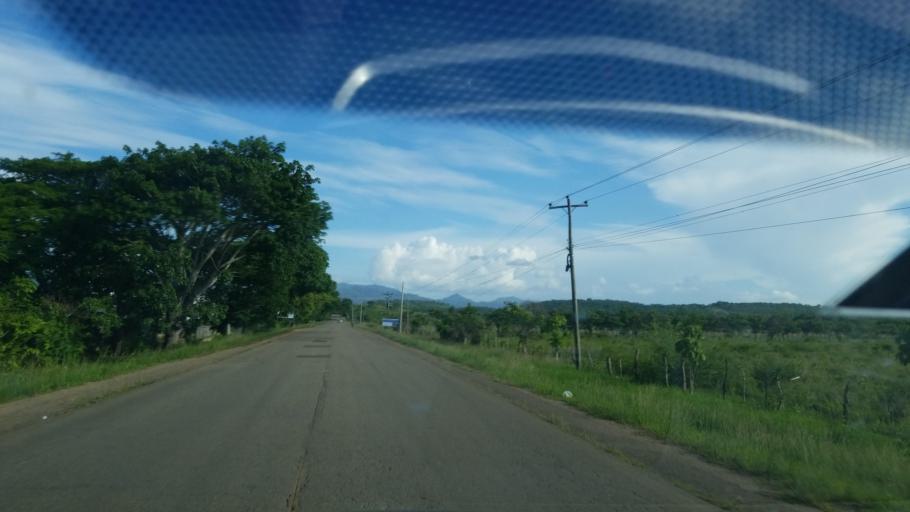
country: HN
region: El Paraiso
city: Arauli
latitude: 13.9353
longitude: -86.5583
